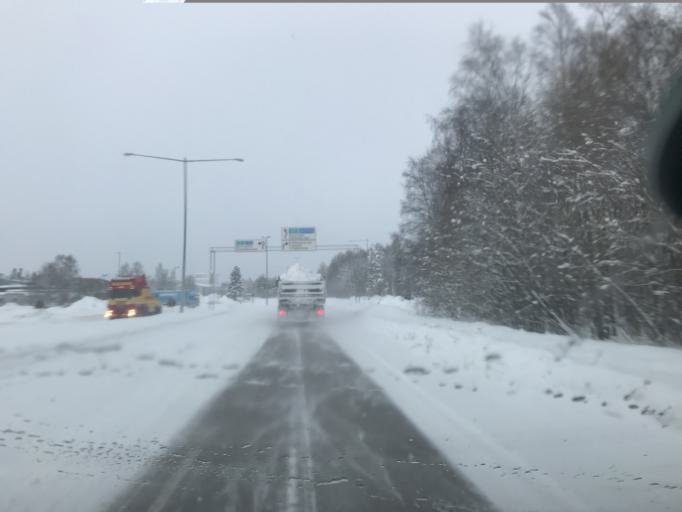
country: SE
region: Norrbotten
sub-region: Lulea Kommun
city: Lulea
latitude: 65.6117
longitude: 22.1352
